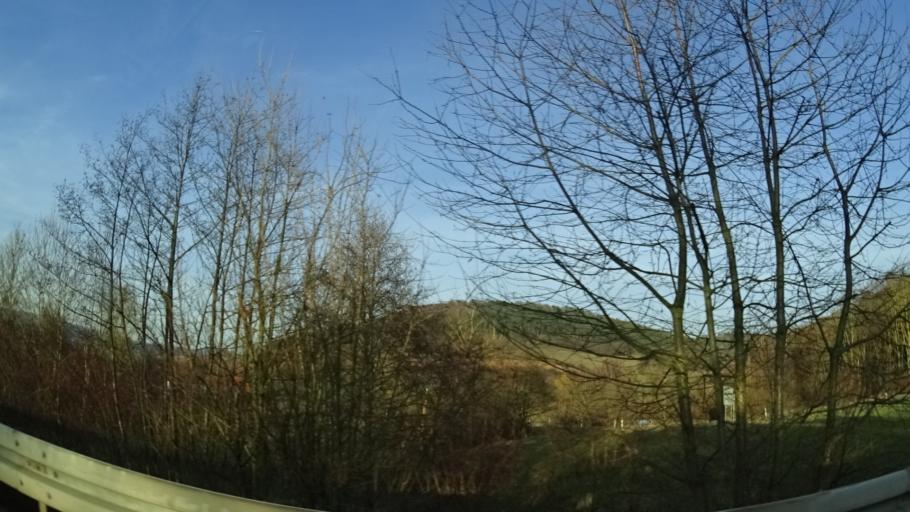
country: DE
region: Hesse
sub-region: Regierungsbezirk Darmstadt
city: Schluchtern
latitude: 50.3262
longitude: 9.5908
